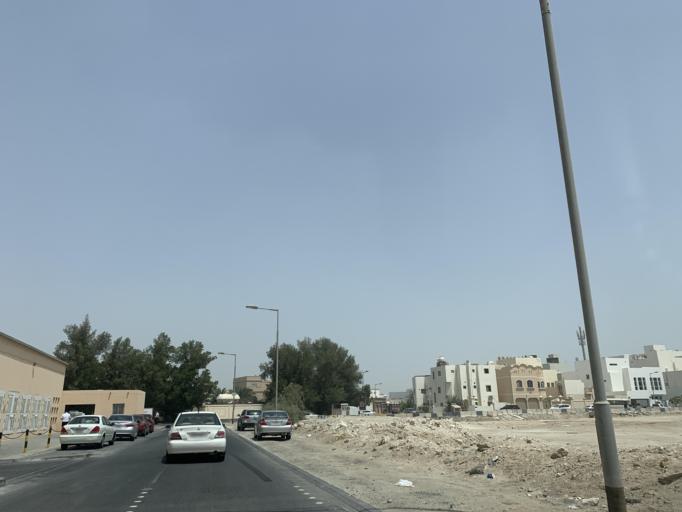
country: BH
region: Northern
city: Madinat `Isa
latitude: 26.1632
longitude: 50.5237
